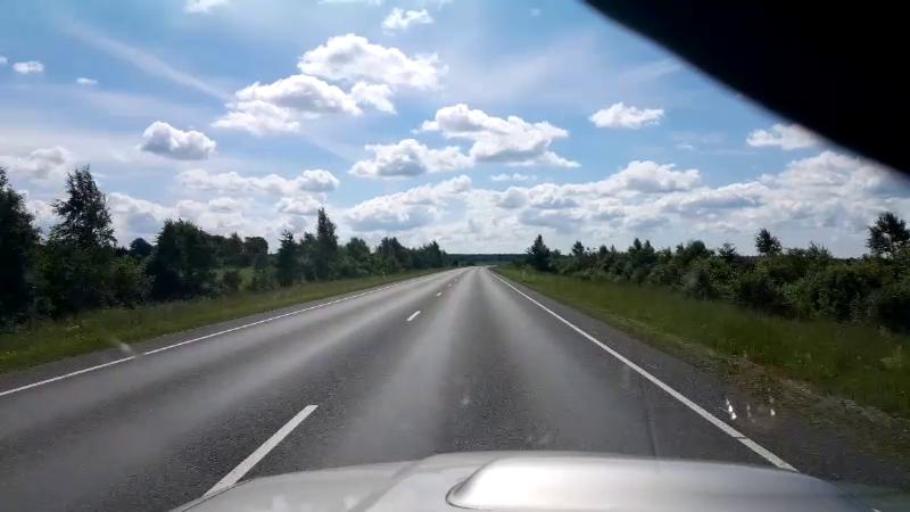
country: EE
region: Jaervamaa
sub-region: Jaerva-Jaani vald
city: Jarva-Jaani
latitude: 59.1545
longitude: 25.7672
